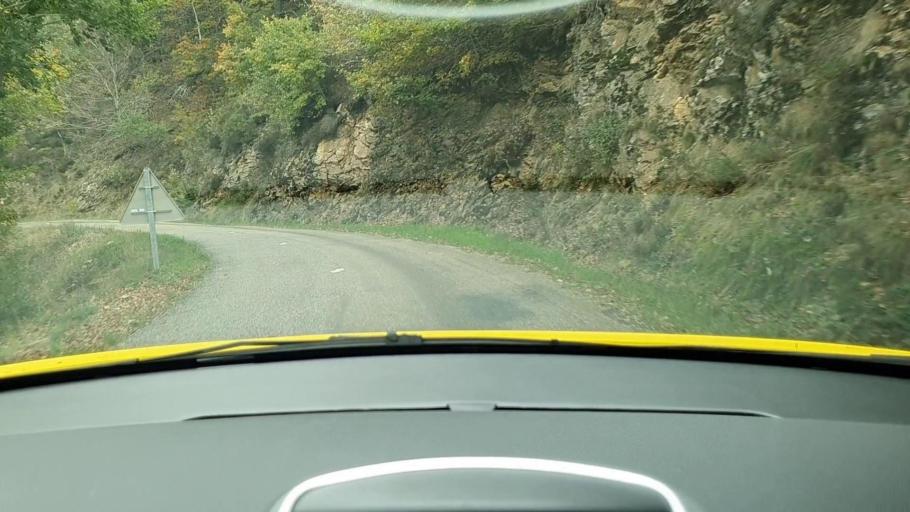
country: FR
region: Languedoc-Roussillon
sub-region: Departement de la Lozere
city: Meyrueis
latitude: 44.0841
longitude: 3.4262
